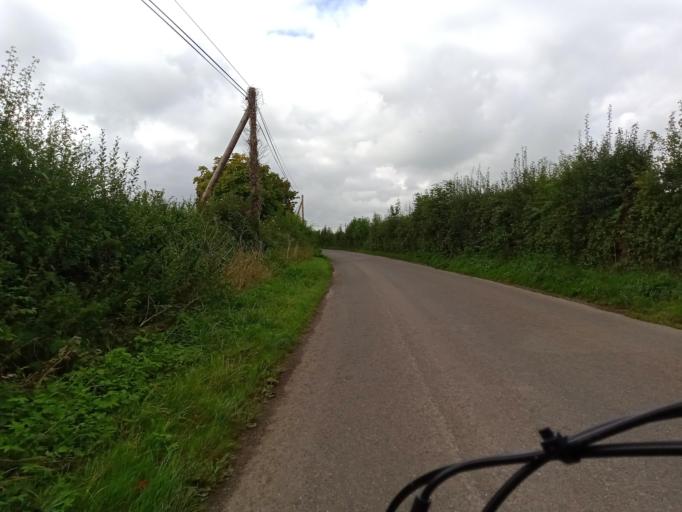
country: IE
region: Leinster
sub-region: Kilkenny
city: Callan
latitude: 52.5365
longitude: -7.2774
